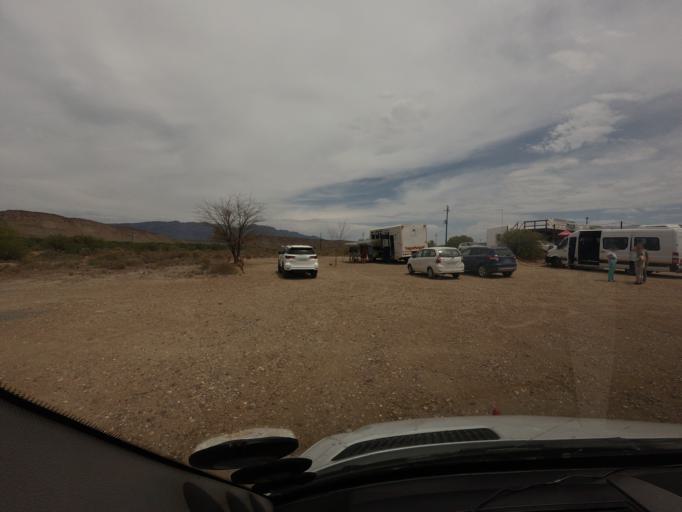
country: ZA
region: Western Cape
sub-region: Eden District Municipality
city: Ladismith
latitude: -33.7791
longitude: 20.9331
